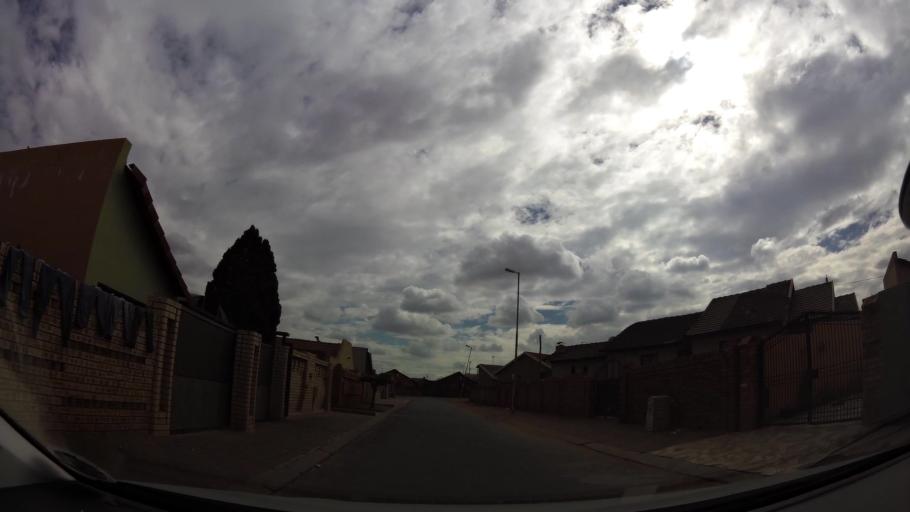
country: ZA
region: Gauteng
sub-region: City of Johannesburg Metropolitan Municipality
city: Soweto
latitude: -26.2826
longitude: 27.8542
